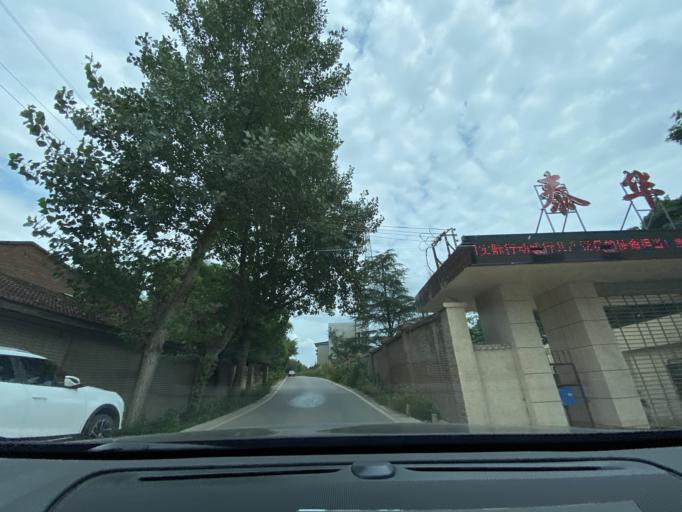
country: CN
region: Sichuan
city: Jiancheng
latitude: 30.4382
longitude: 104.5350
